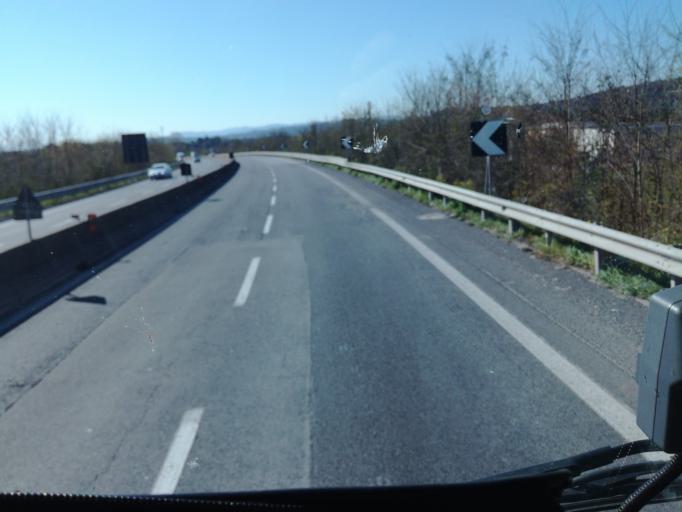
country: IT
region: Umbria
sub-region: Provincia di Perugia
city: Ponte Felcino
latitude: 43.1184
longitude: 12.4516
